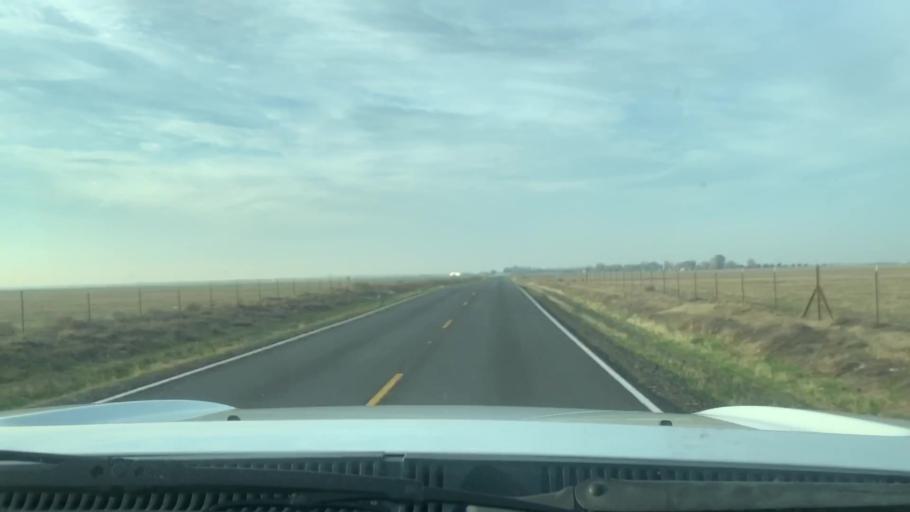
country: US
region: California
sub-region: Kern County
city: Lost Hills
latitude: 35.6021
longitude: -119.8519
